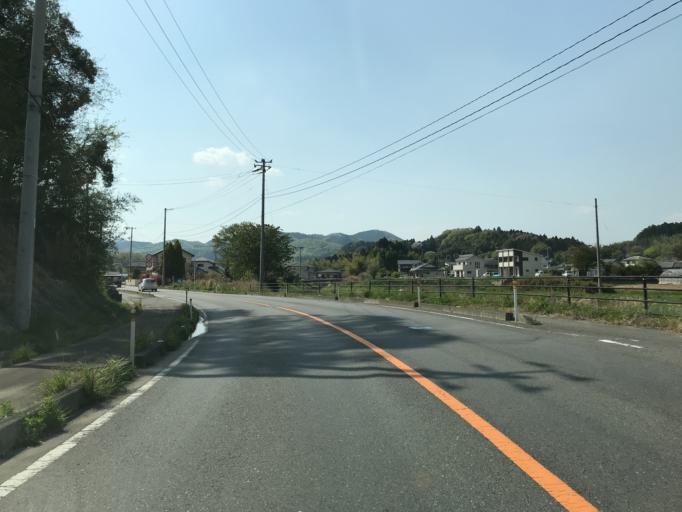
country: JP
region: Fukushima
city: Iwaki
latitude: 36.9516
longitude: 140.7677
